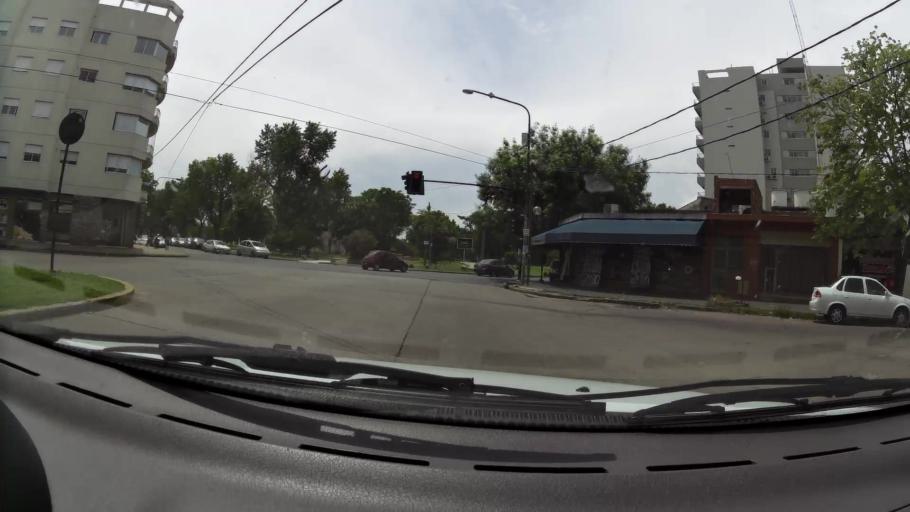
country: AR
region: Buenos Aires
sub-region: Partido de La Plata
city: La Plata
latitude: -34.9449
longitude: -57.9531
